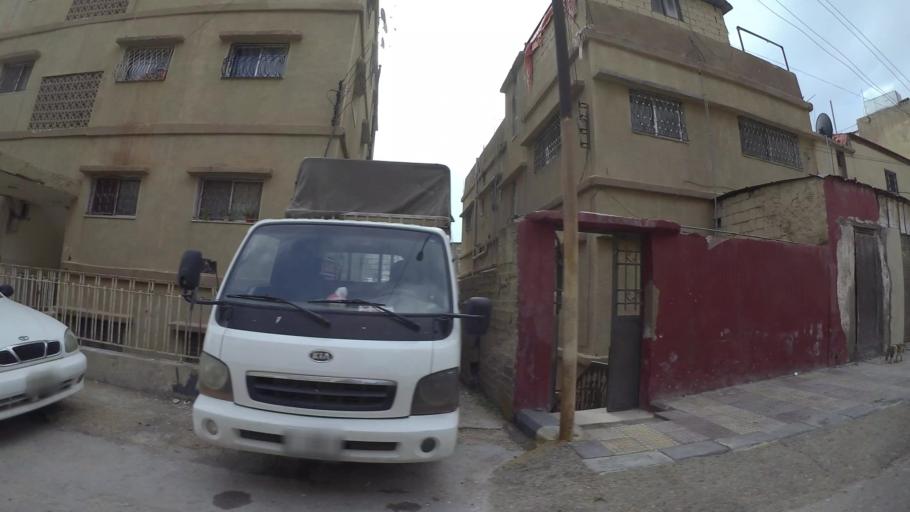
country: JO
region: Amman
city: Amman
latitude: 31.9609
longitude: 35.9340
